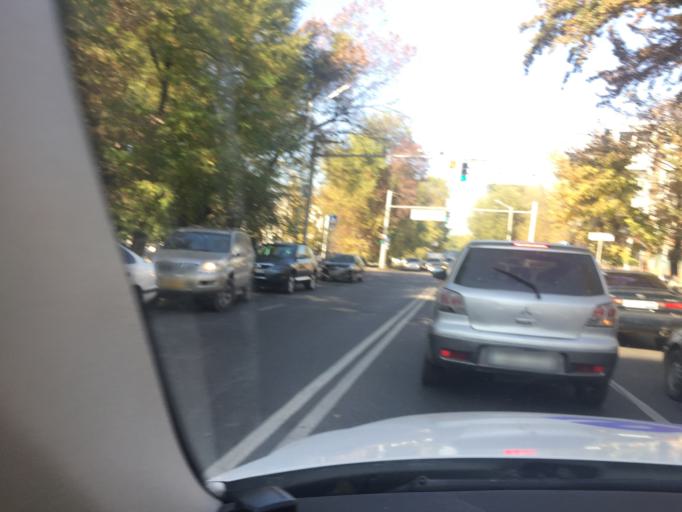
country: KZ
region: Almaty Qalasy
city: Almaty
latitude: 43.2570
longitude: 76.9110
